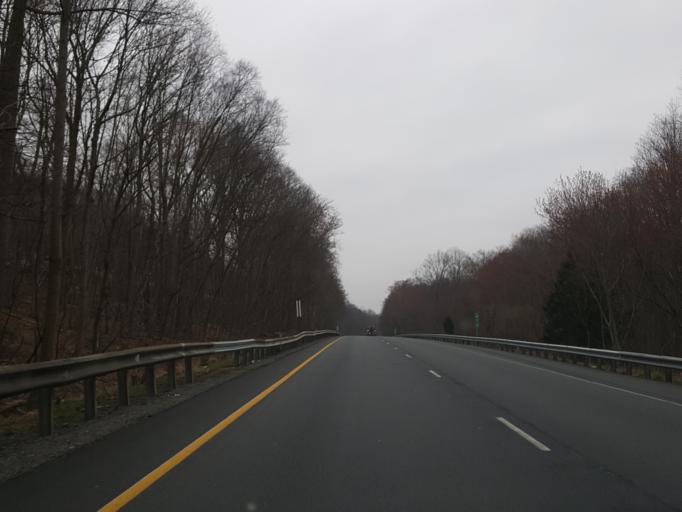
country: US
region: Pennsylvania
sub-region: Schuylkill County
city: Pine Grove
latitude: 40.5210
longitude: -76.4542
